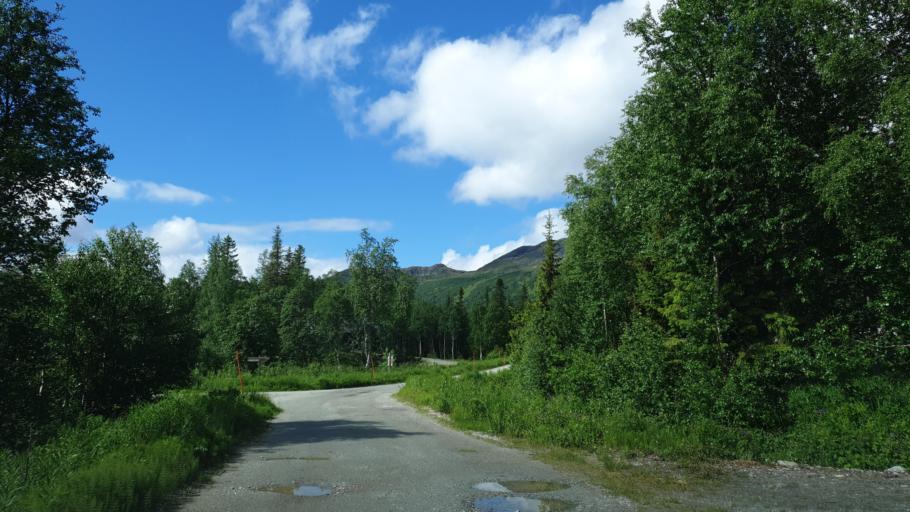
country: SE
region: Vaesterbotten
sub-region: Vilhelmina Kommun
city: Sjoberg
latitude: 65.2515
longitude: 15.5166
